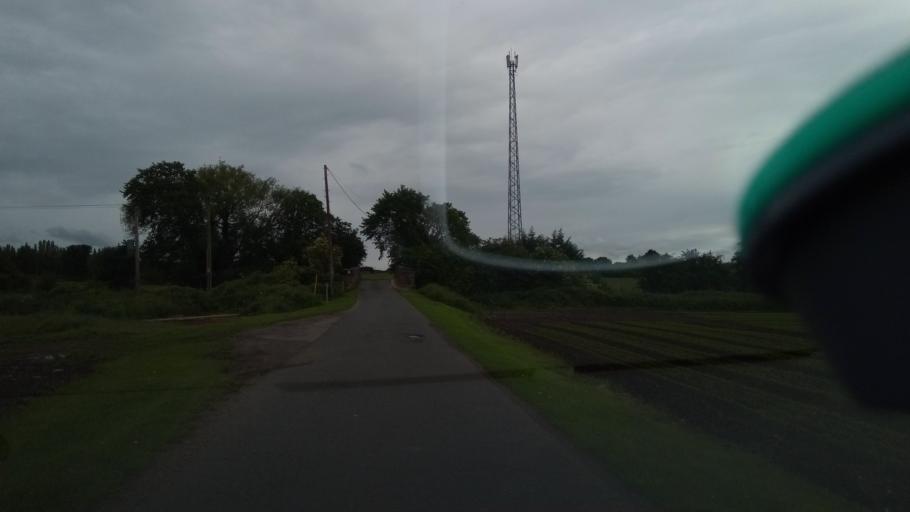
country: GB
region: England
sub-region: Derbyshire
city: Melbourne
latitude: 52.8488
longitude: -1.4157
